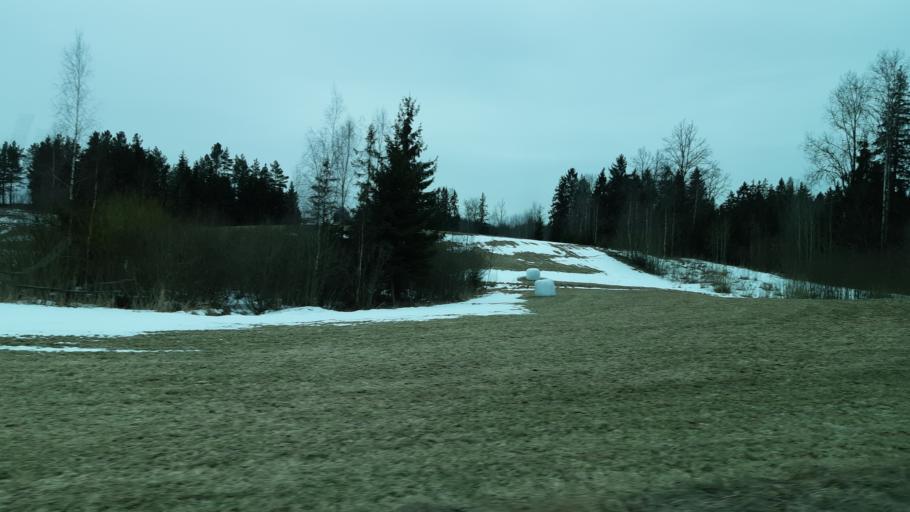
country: LT
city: Virbalis
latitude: 54.3796
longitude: 22.8175
